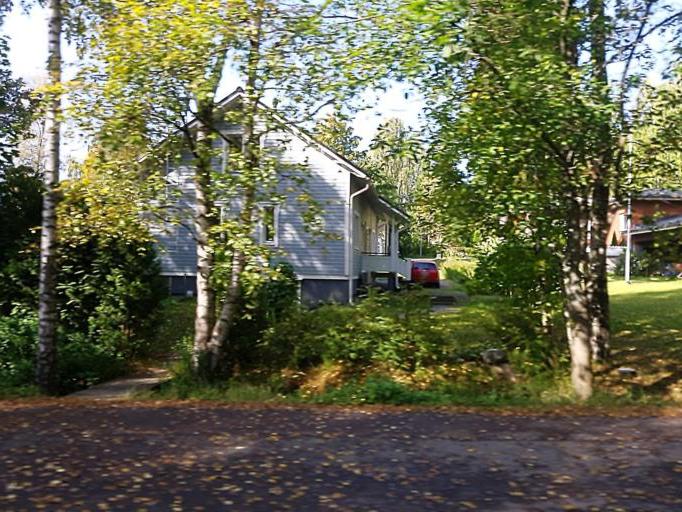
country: FI
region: Uusimaa
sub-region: Helsinki
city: Teekkarikylae
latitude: 60.2503
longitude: 24.8958
